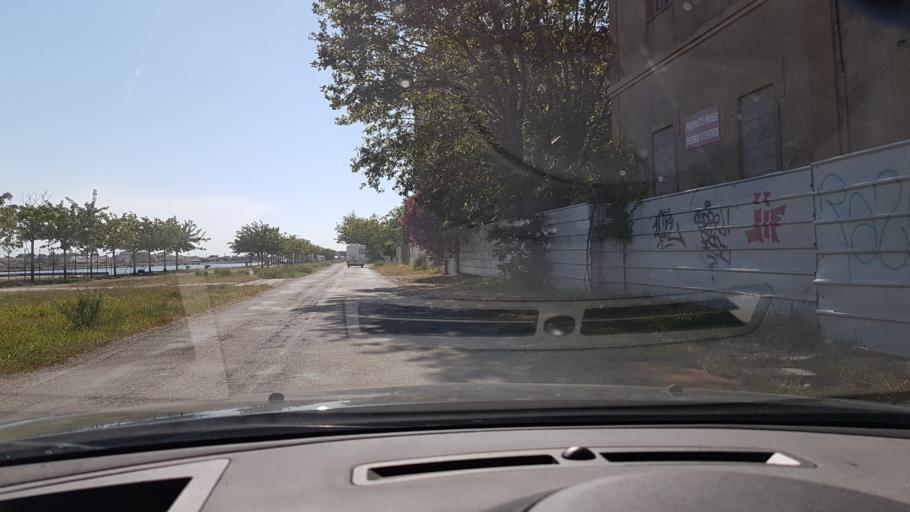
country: FR
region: Provence-Alpes-Cote d'Azur
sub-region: Departement des Bouches-du-Rhone
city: Port-Saint-Louis-du-Rhone
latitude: 43.3868
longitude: 4.8210
